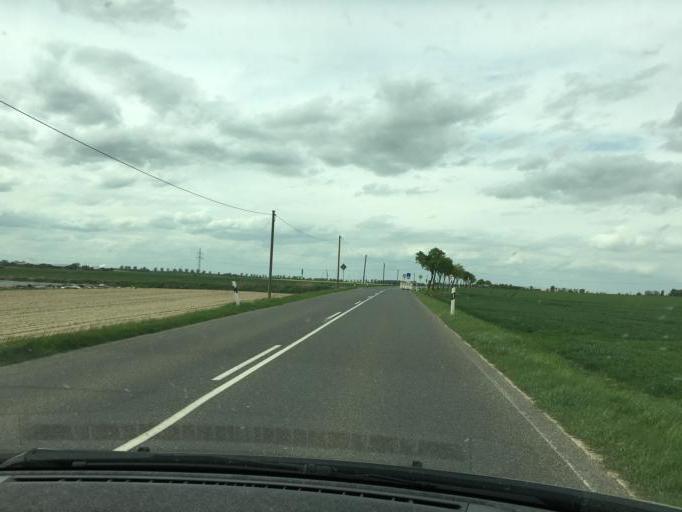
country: DE
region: North Rhine-Westphalia
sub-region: Regierungsbezirk Koln
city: Vettweiss
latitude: 50.7756
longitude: 6.5901
